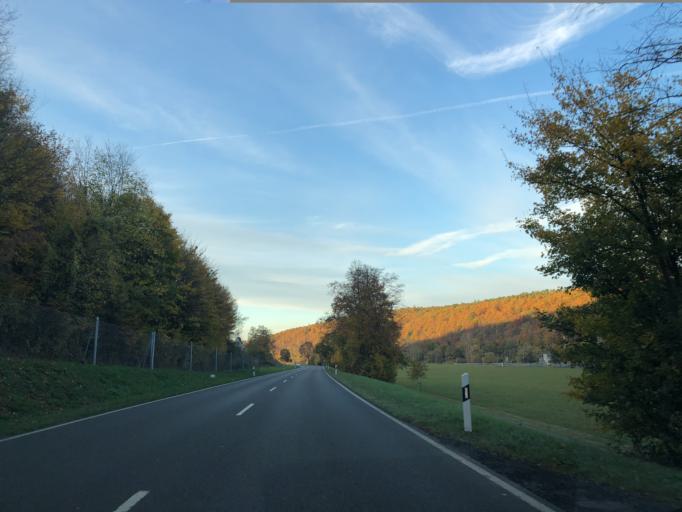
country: DE
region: Bavaria
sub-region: Regierungsbezirk Unterfranken
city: Kreuzwertheim
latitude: 49.7555
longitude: 9.5504
